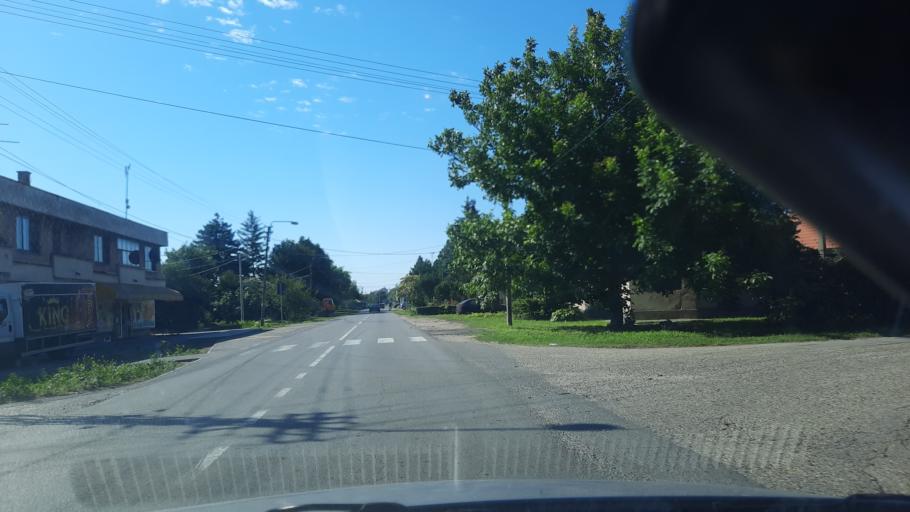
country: RS
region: Autonomna Pokrajina Vojvodina
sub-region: Juznobanatski Okrug
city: Kovin
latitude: 44.7509
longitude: 20.9700
